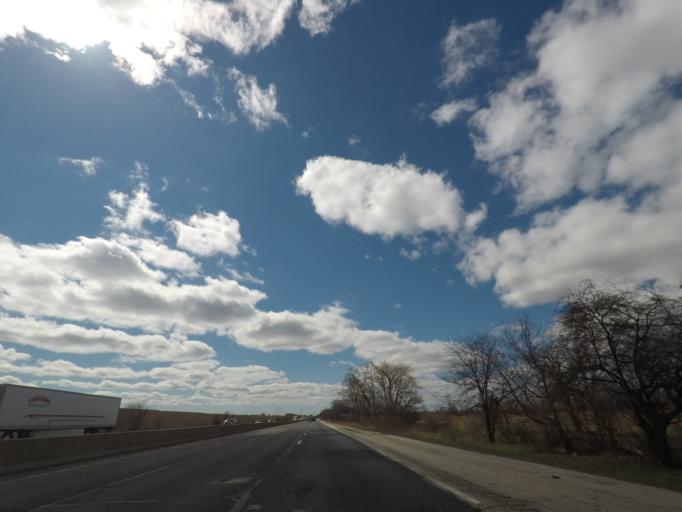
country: US
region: Illinois
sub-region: Will County
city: Crystal Lawns
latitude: 41.6084
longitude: -88.1634
